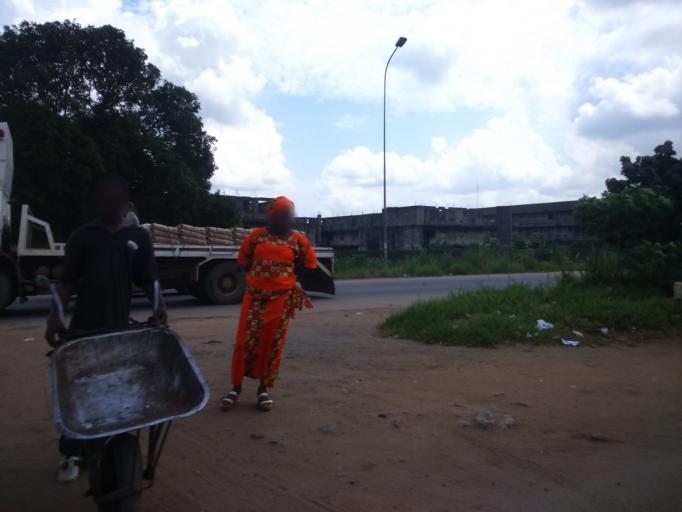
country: CI
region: Lagunes
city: Abobo
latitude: 5.3610
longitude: -4.0847
